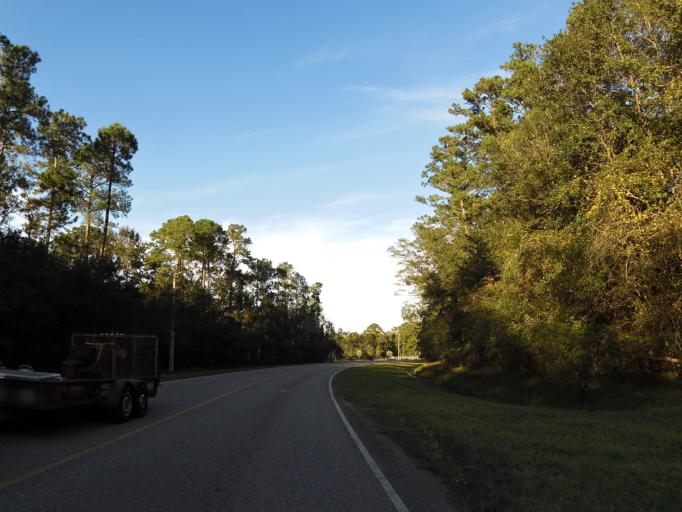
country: US
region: Florida
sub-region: Duval County
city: Jacksonville
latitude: 30.3260
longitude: -81.7706
